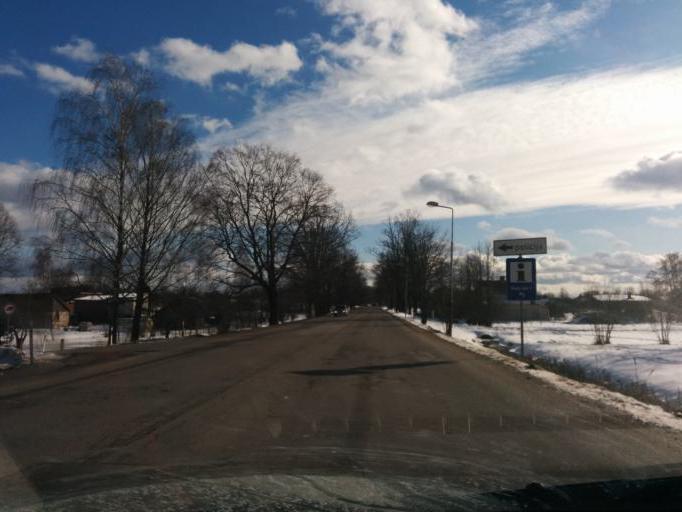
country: LV
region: Gulbenes Rajons
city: Gulbene
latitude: 57.1714
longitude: 26.7497
